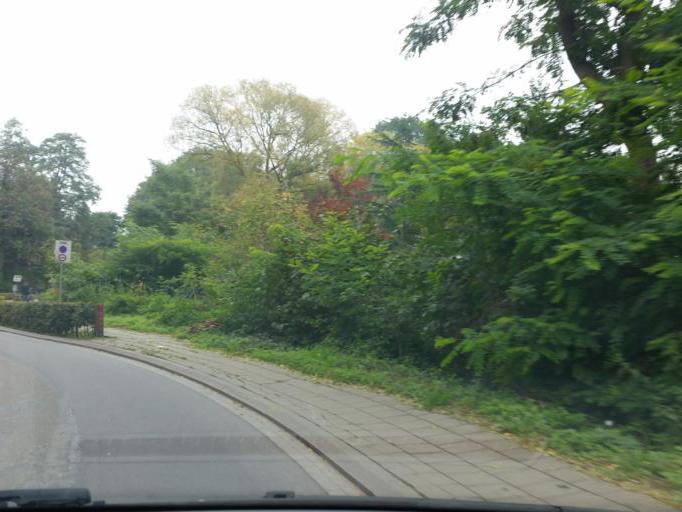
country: BE
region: Flanders
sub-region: Provincie Vlaams-Brabant
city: Beersel
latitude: 50.7658
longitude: 4.3022
